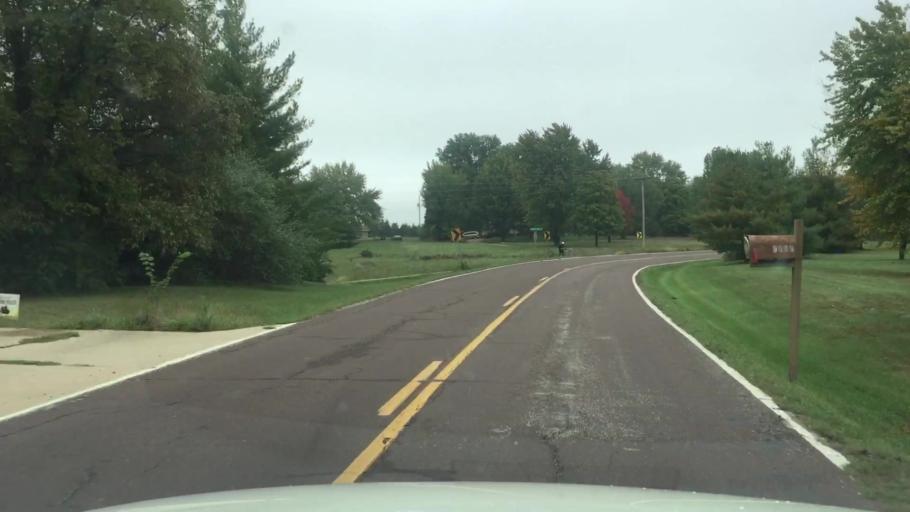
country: US
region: Missouri
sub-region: Boone County
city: Ashland
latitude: 38.8370
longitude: -92.3466
